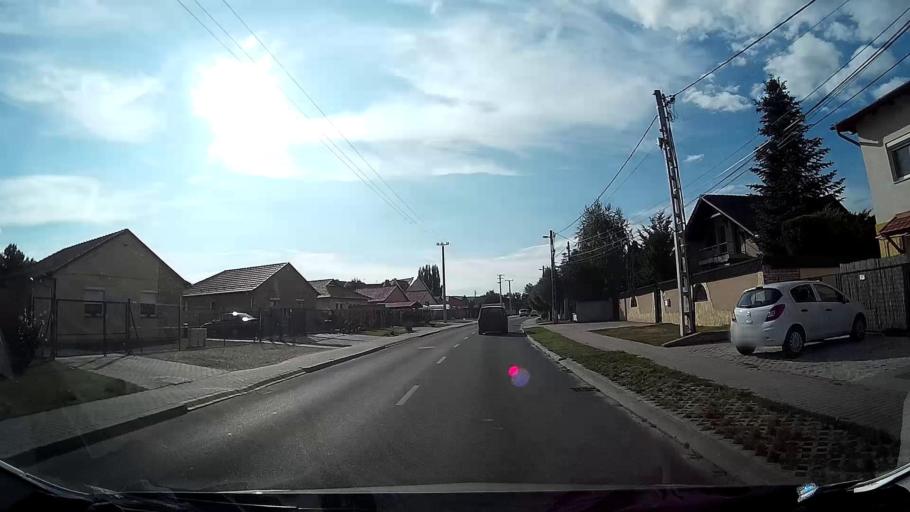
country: HU
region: Pest
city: Nagykovacsi
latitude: 47.6465
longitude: 19.0203
